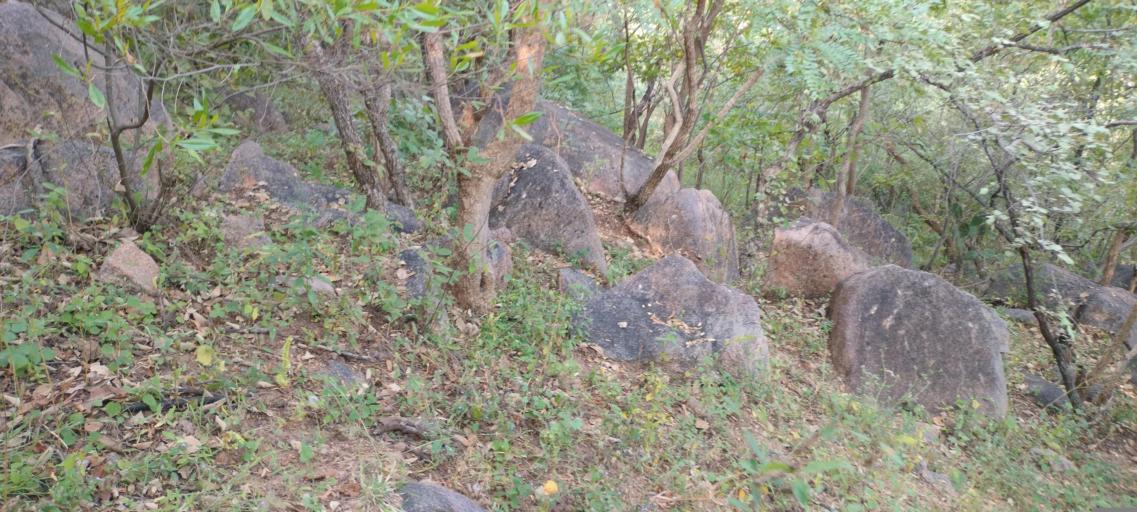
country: IN
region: Telangana
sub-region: Mahbubnagar
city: Farrukhnagar
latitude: 16.8934
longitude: 78.4956
